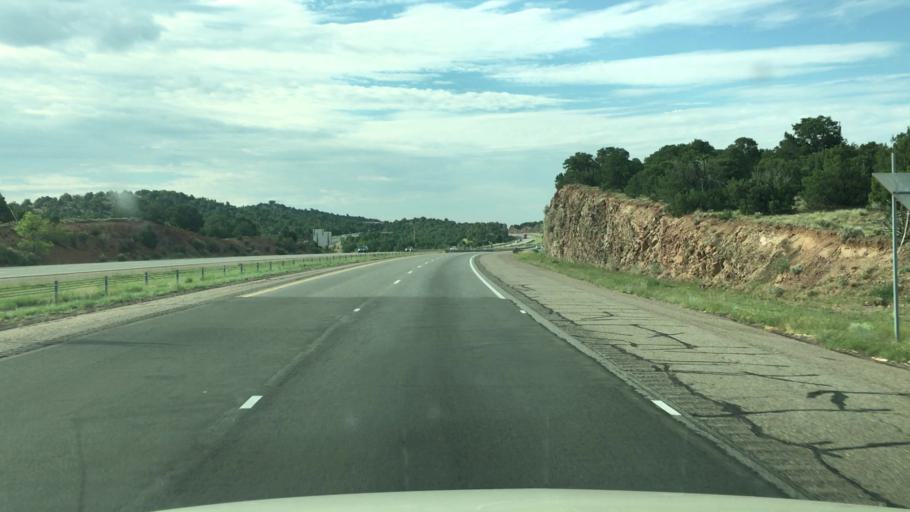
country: US
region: New Mexico
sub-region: Santa Fe County
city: Santa Fe
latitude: 35.6245
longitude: -105.9209
